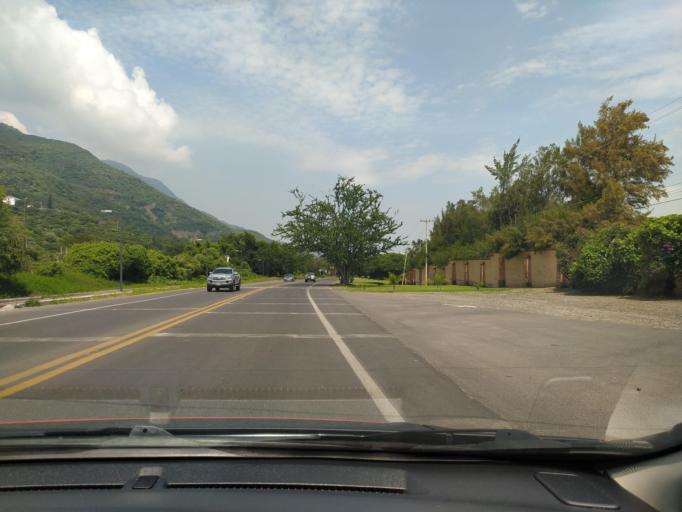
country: MX
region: Jalisco
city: San Juan Cosala
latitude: 20.2943
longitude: -103.3845
